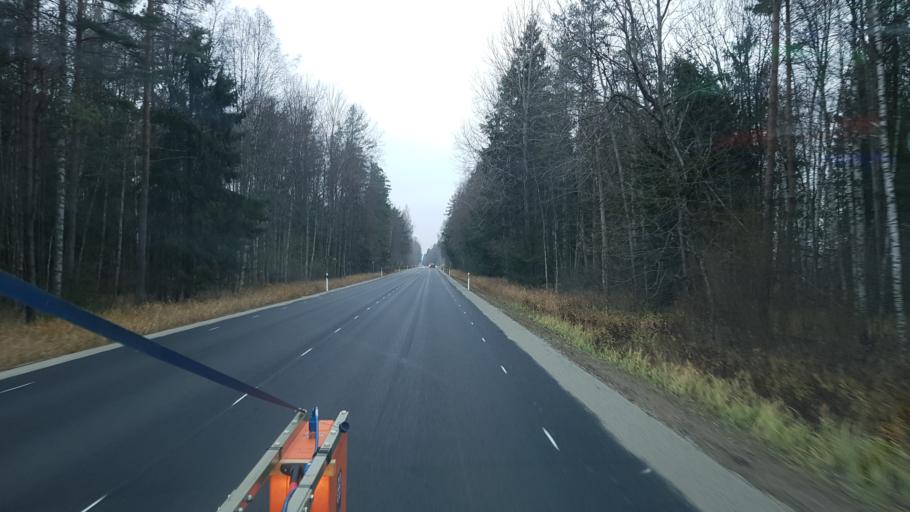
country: EE
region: Paernumaa
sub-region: Vaendra vald (alev)
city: Vandra
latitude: 58.8426
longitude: 25.0575
